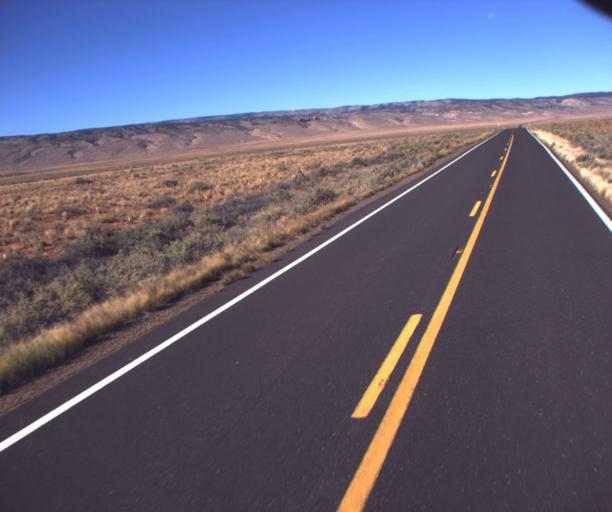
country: US
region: Arizona
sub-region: Coconino County
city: Page
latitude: 36.7126
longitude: -111.9800
